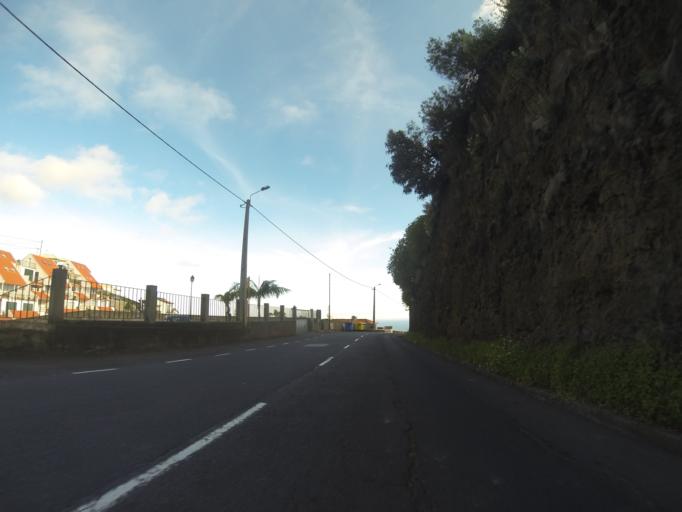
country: PT
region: Madeira
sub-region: Funchal
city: Nossa Senhora do Monte
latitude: 32.6609
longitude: -16.8843
